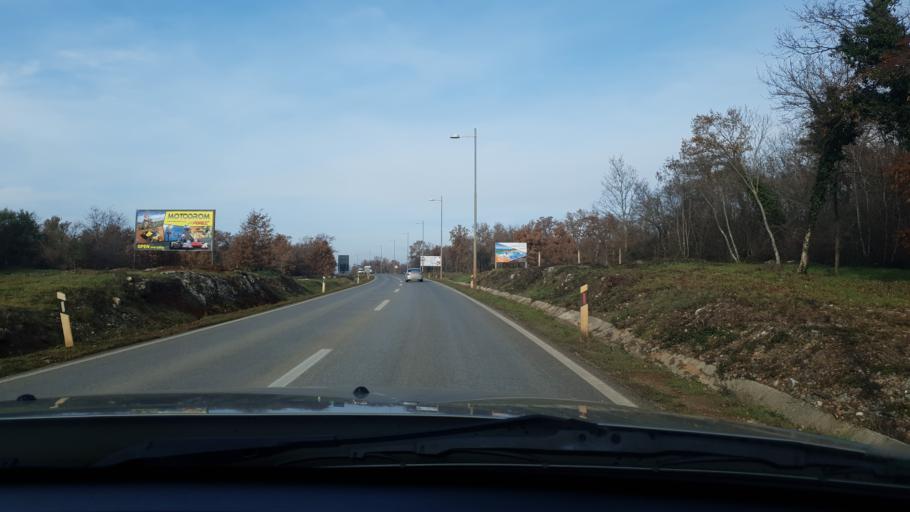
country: HR
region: Istarska
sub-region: Grad Porec
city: Porec
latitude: 45.2451
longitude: 13.6252
